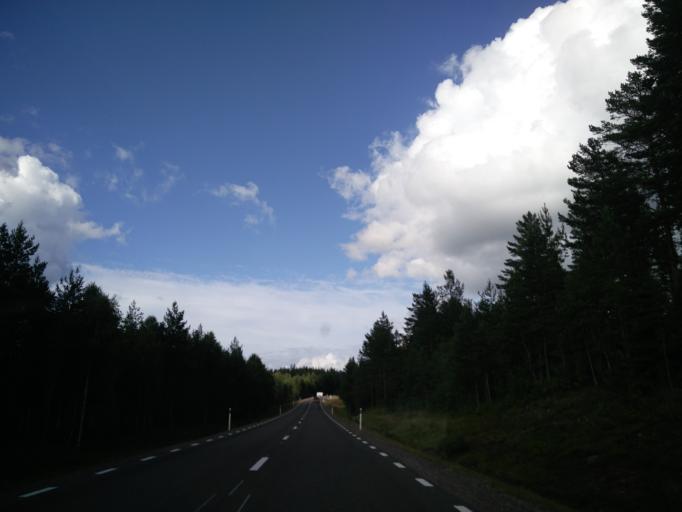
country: SE
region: Vaermland
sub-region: Torsby Kommun
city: Torsby
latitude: 60.3707
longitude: 13.2038
